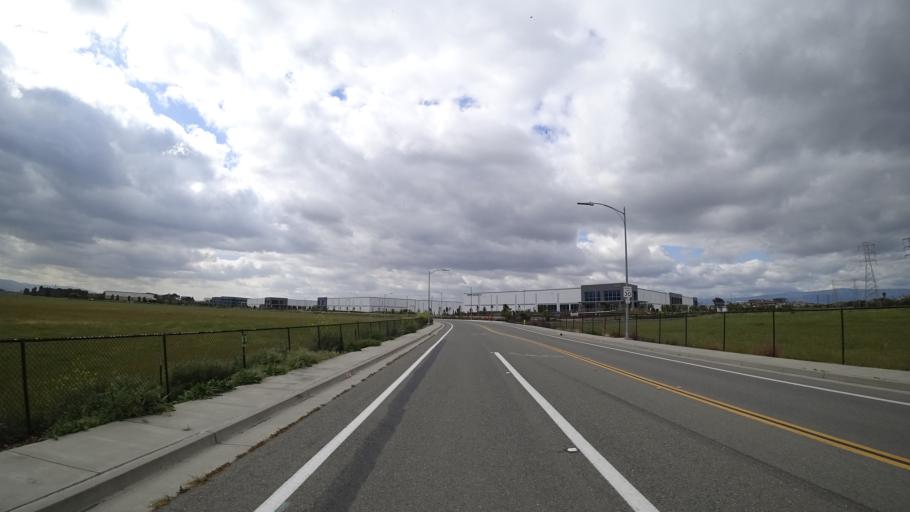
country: US
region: California
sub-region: Santa Clara County
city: Milpitas
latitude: 37.4296
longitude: -121.9654
